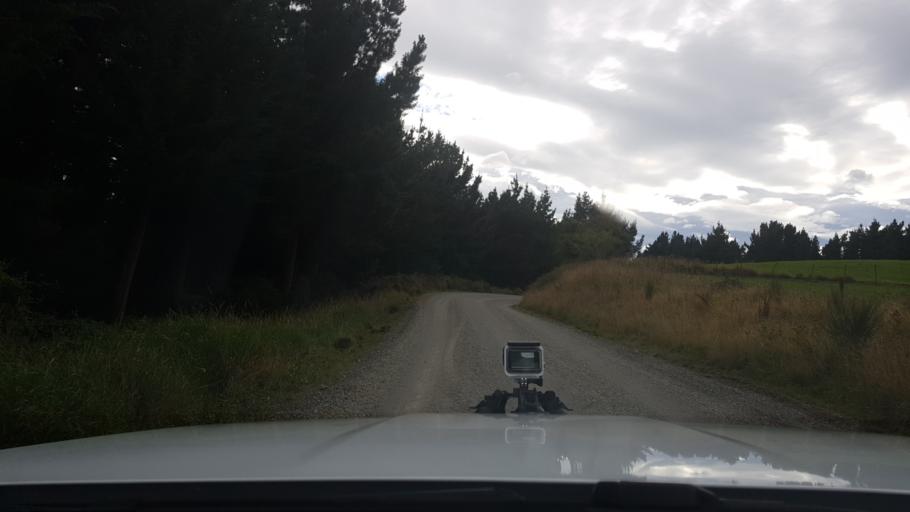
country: NZ
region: Otago
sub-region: Clutha District
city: Balclutha
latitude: -46.2191
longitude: 169.7359
